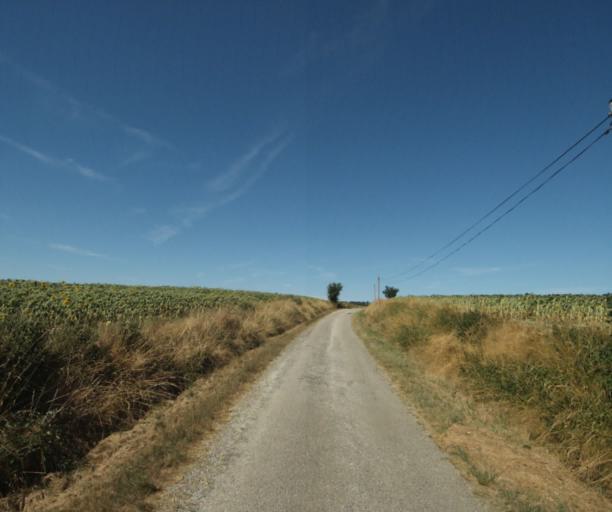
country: FR
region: Midi-Pyrenees
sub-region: Departement de la Haute-Garonne
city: Saint-Felix-Lauragais
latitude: 43.5058
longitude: 1.9034
